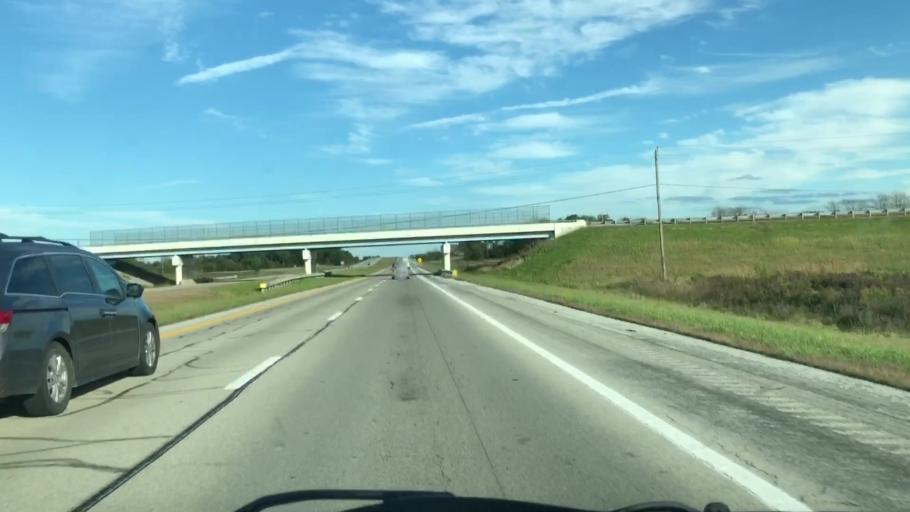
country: US
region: Ohio
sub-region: Allen County
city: Lima
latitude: 40.8230
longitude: -84.0954
